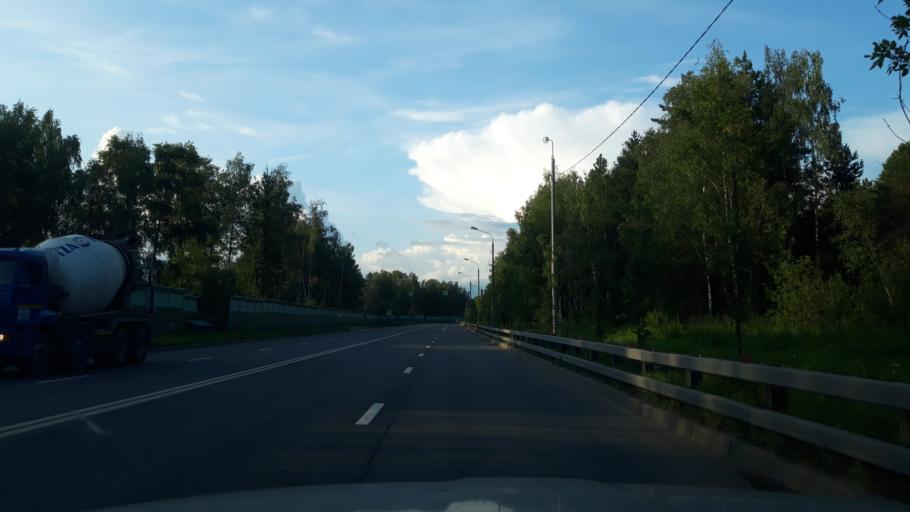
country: RU
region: Moskovskaya
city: Alabushevo
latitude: 56.0001
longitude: 37.1627
